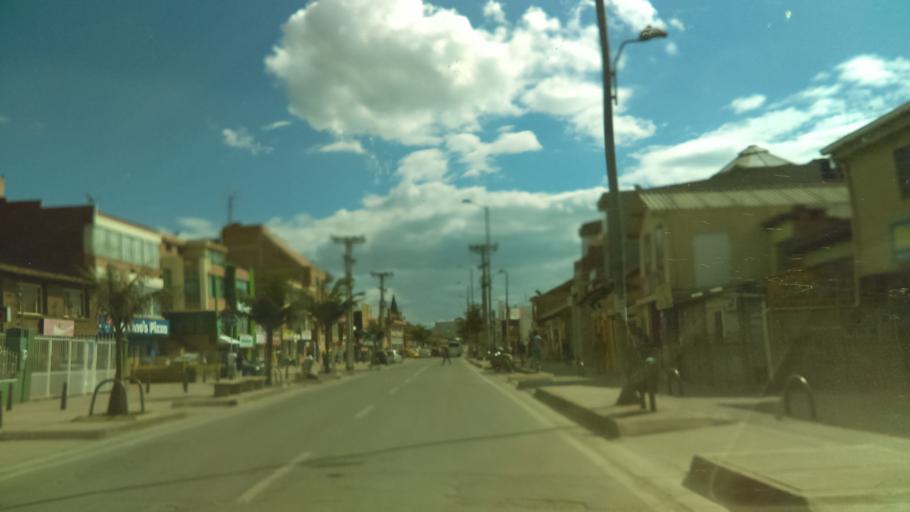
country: CO
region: Cundinamarca
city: Cajica
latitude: 4.9218
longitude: -74.0251
